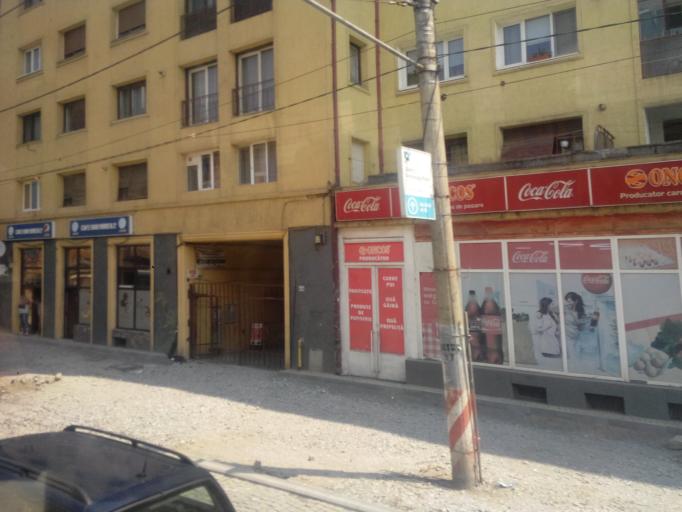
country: RO
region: Cluj
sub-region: Municipiul Cluj-Napoca
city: Cluj-Napoca
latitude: 46.7829
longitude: 23.5877
